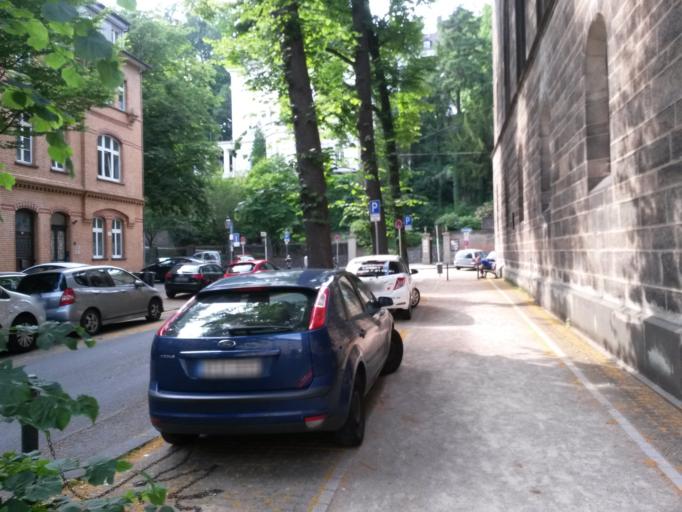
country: DE
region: North Rhine-Westphalia
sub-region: Regierungsbezirk Dusseldorf
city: Wuppertal
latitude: 51.2550
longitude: 7.1350
